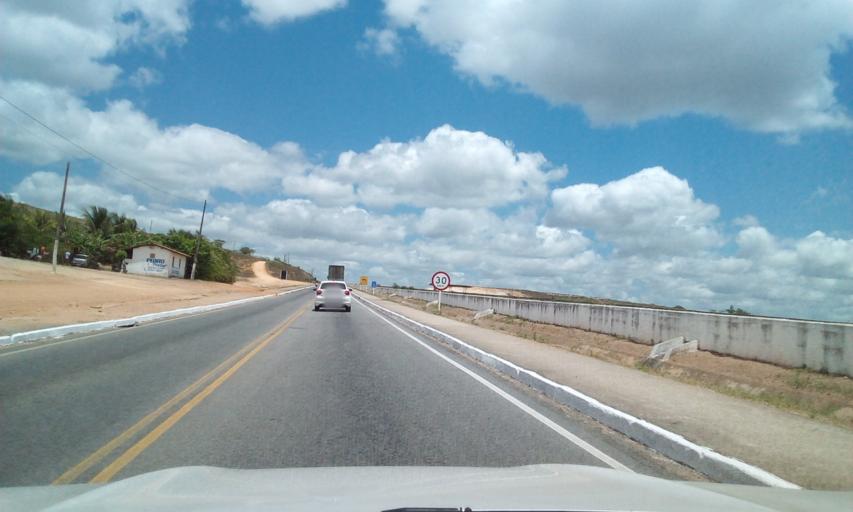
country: BR
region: Alagoas
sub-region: Junqueiro
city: Junqueiro
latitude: -9.9099
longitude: -36.4703
